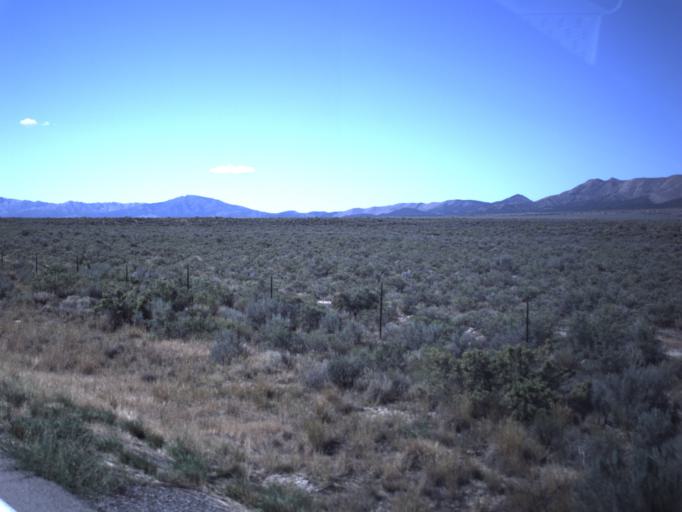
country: US
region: Utah
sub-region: Tooele County
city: Tooele
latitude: 40.2309
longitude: -112.4033
